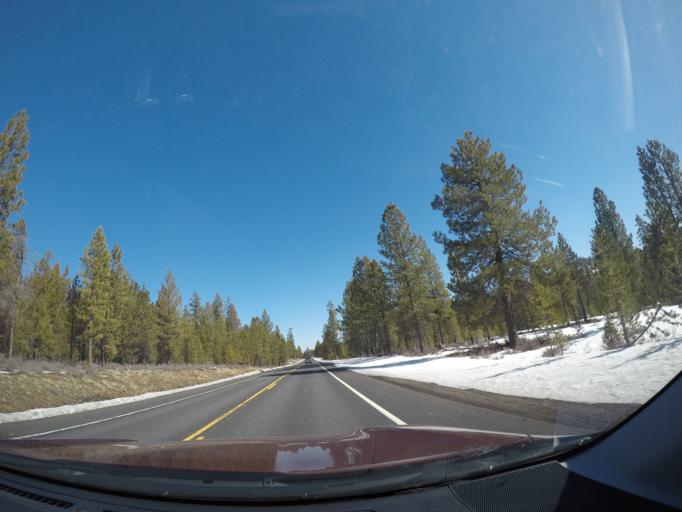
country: US
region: Oregon
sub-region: Deschutes County
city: Three Rivers
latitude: 43.8580
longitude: -121.5062
